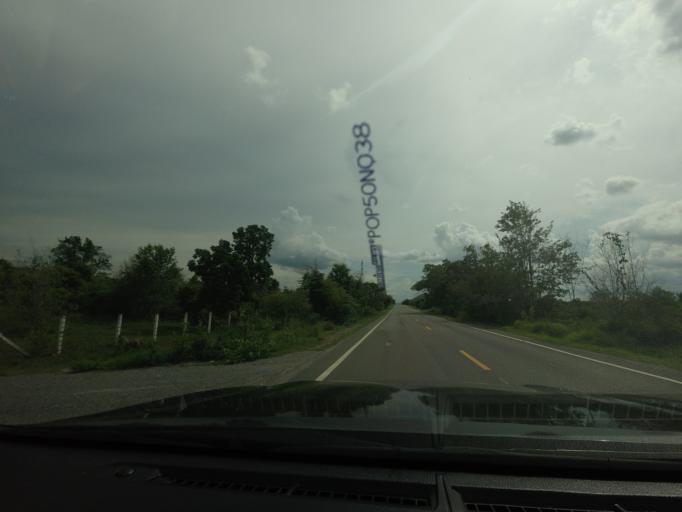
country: TH
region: Kanchanaburi
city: Bo Phloi
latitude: 14.1648
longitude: 99.4323
